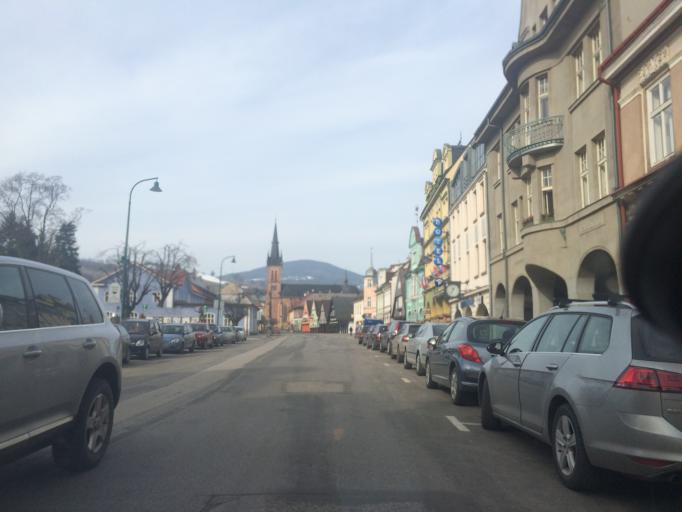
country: CZ
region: Kralovehradecky
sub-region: Okres Trutnov
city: Vrchlabi
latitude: 50.6274
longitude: 15.6108
